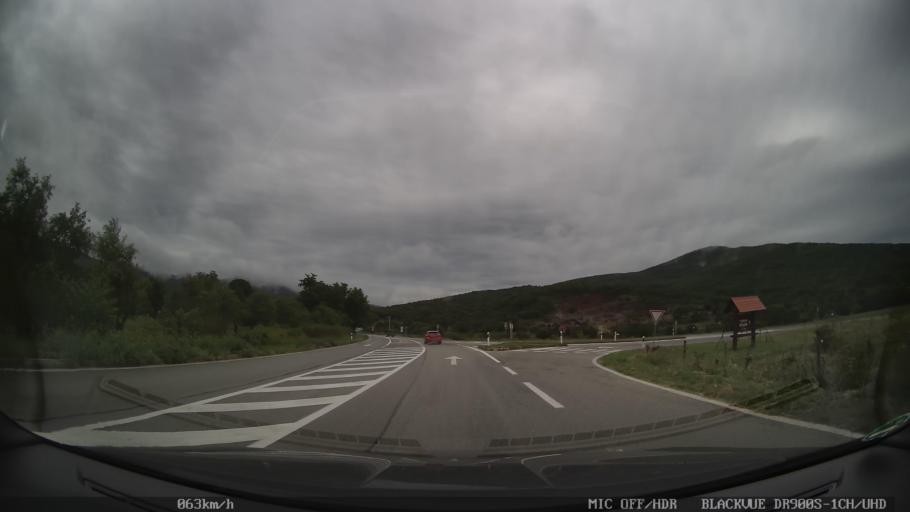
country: HR
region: Licko-Senjska
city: Otocac
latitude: 44.8553
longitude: 15.3349
